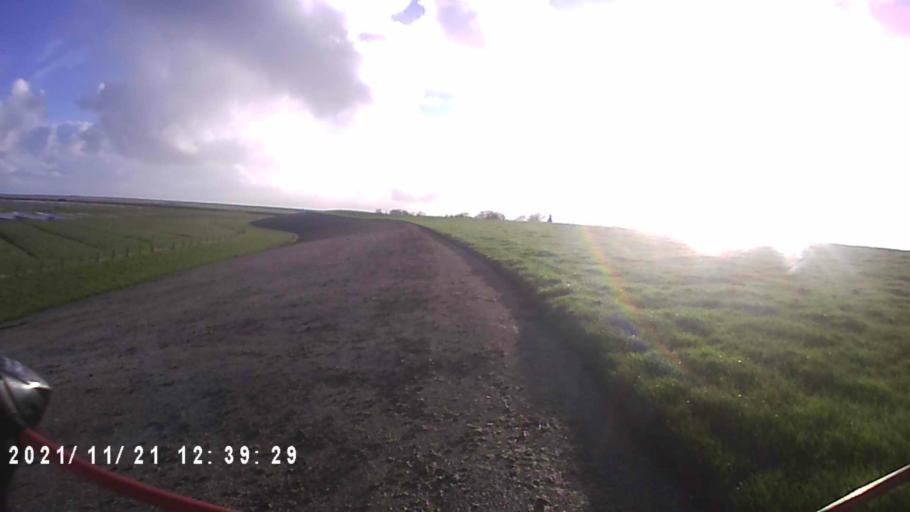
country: NL
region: Friesland
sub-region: Gemeente Dongeradeel
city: Anjum
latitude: 53.4046
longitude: 6.0805
